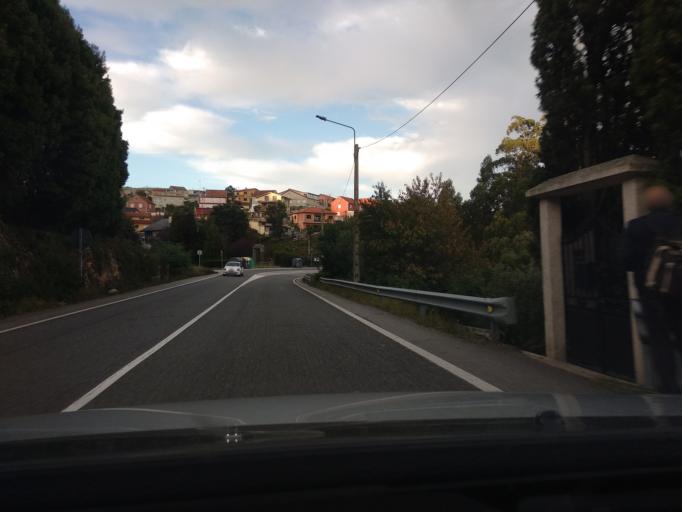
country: ES
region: Galicia
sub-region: Provincia de Pontevedra
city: Vigo
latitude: 42.2812
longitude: -8.6901
